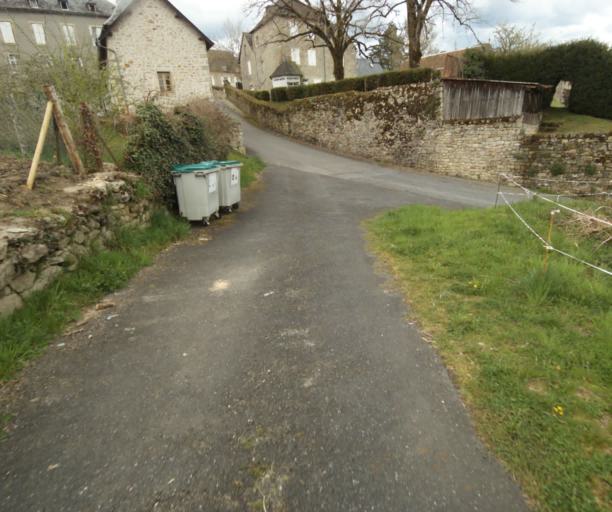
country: FR
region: Limousin
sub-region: Departement de la Correze
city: Argentat
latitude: 45.1952
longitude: 1.9706
